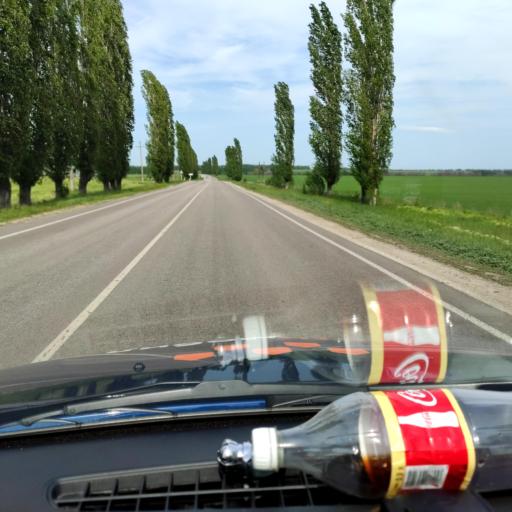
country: RU
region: Voronezj
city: Novaya Usman'
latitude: 51.5449
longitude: 39.3584
